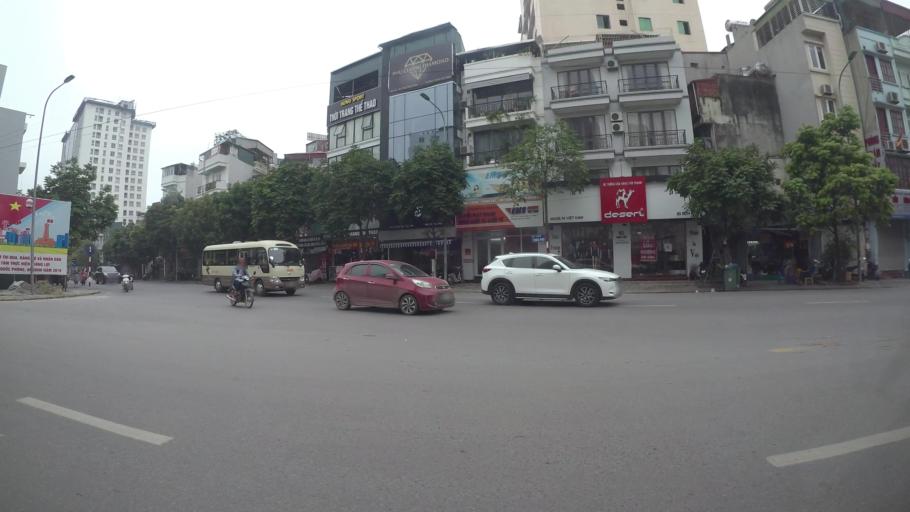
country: VN
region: Ha Noi
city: Dong Da
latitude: 21.0330
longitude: 105.8305
